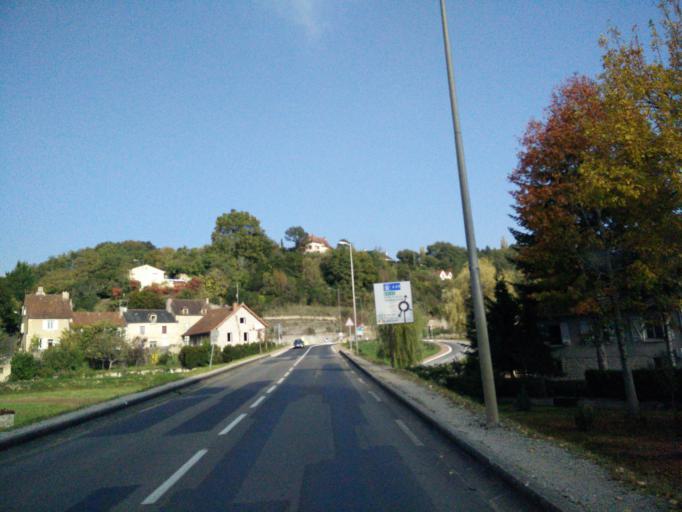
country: FR
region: Aquitaine
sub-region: Departement de la Dordogne
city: Montignac
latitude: 45.0687
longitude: 1.1660
